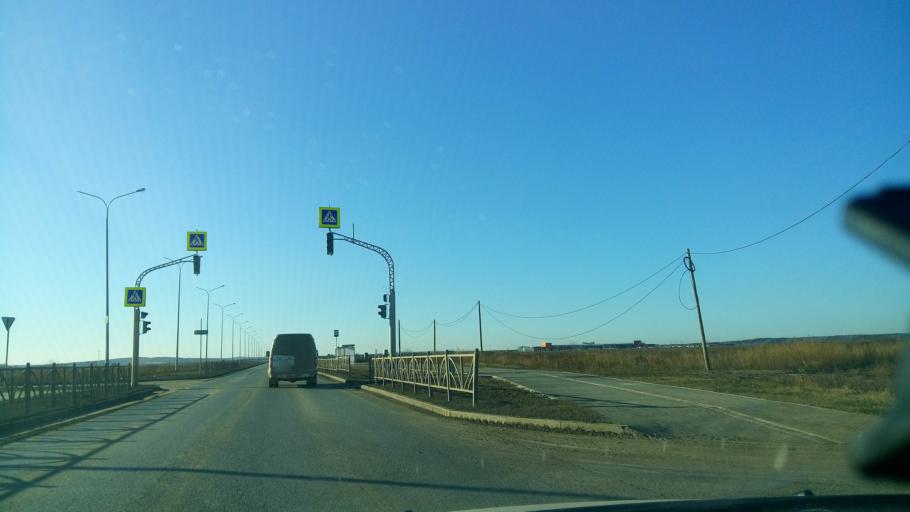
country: RU
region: Sverdlovsk
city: Sovkhoznyy
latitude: 56.7417
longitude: 60.5626
